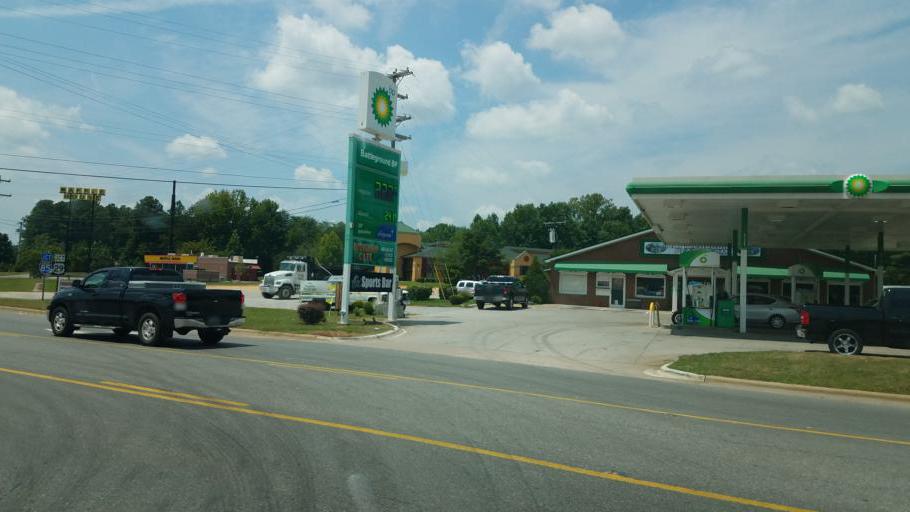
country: US
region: North Carolina
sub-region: Cleveland County
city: Kings Mountain
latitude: 35.2283
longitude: -81.3330
